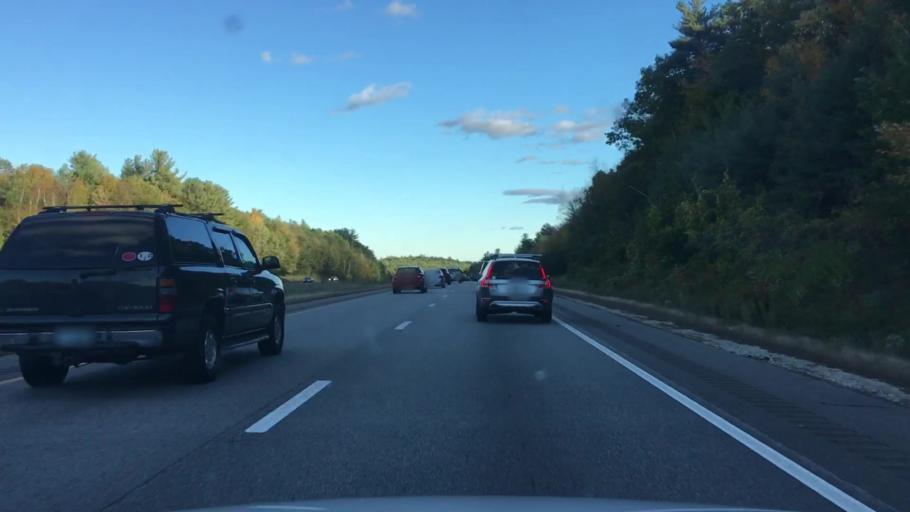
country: US
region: New Hampshire
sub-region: Rockingham County
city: Raymond
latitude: 43.0254
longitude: -71.2375
